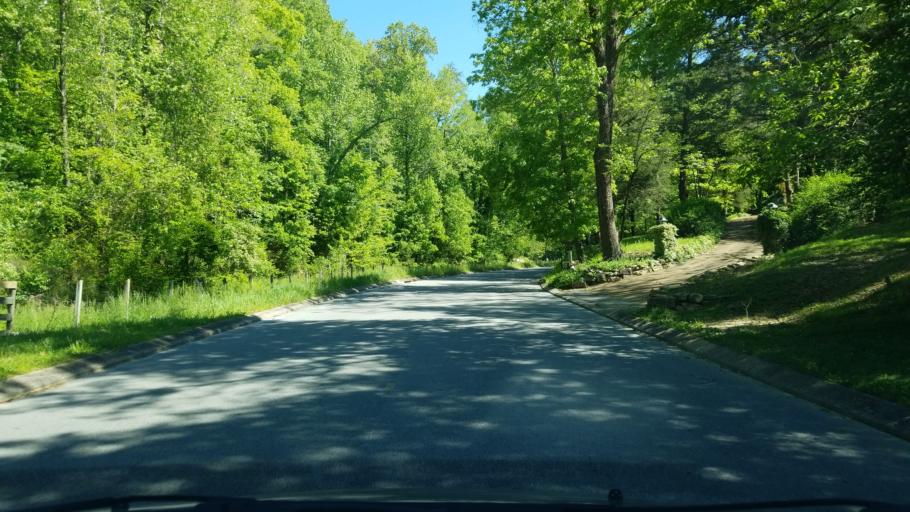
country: US
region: Tennessee
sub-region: Hamilton County
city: Walden
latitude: 35.1434
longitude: -85.3008
